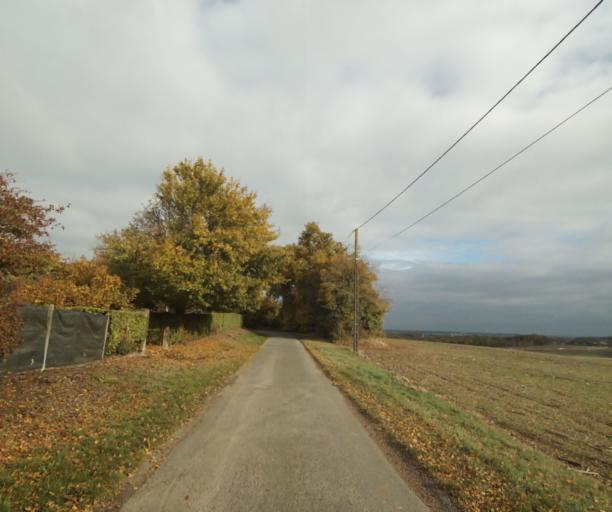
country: FR
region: Poitou-Charentes
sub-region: Departement de la Charente-Maritime
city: Saint-Georges-des-Coteaux
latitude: 45.7658
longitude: -0.6847
